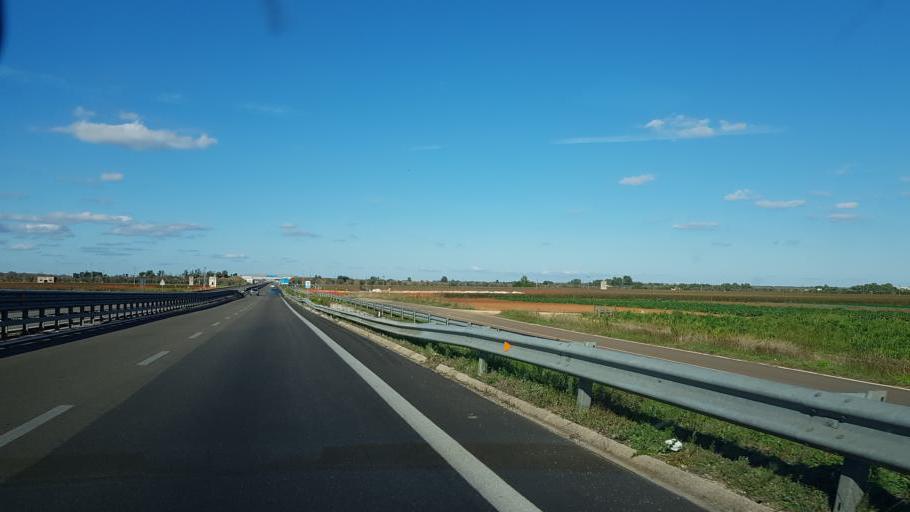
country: IT
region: Apulia
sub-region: Provincia di Lecce
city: Collemeto
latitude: 40.2509
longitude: 18.1158
